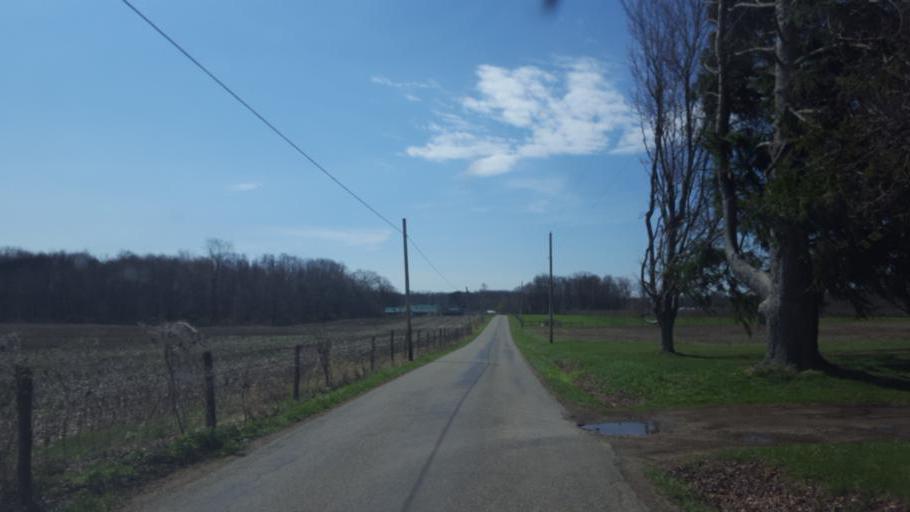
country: US
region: Ohio
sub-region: Knox County
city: Gambier
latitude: 40.3653
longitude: -82.4381
